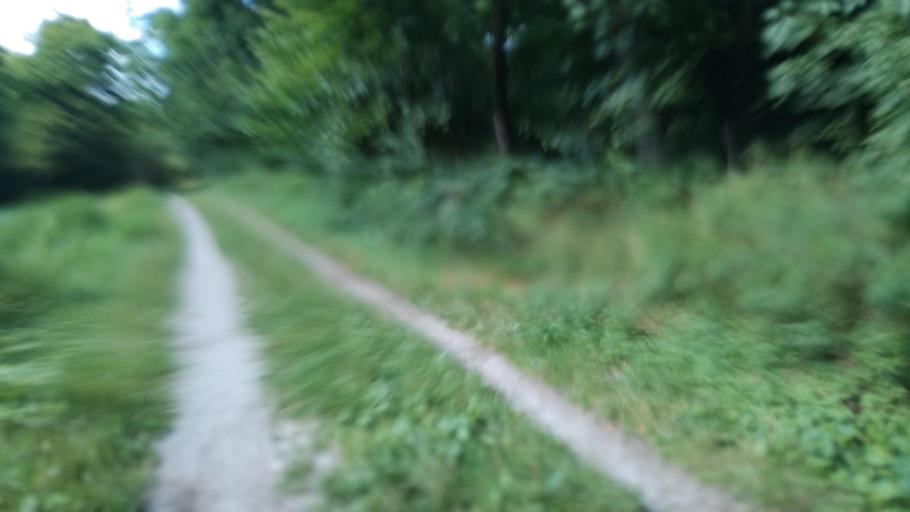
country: DE
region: Baden-Wuerttemberg
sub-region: Karlsruhe Region
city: Ettlingen
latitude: 48.9733
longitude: 8.3881
